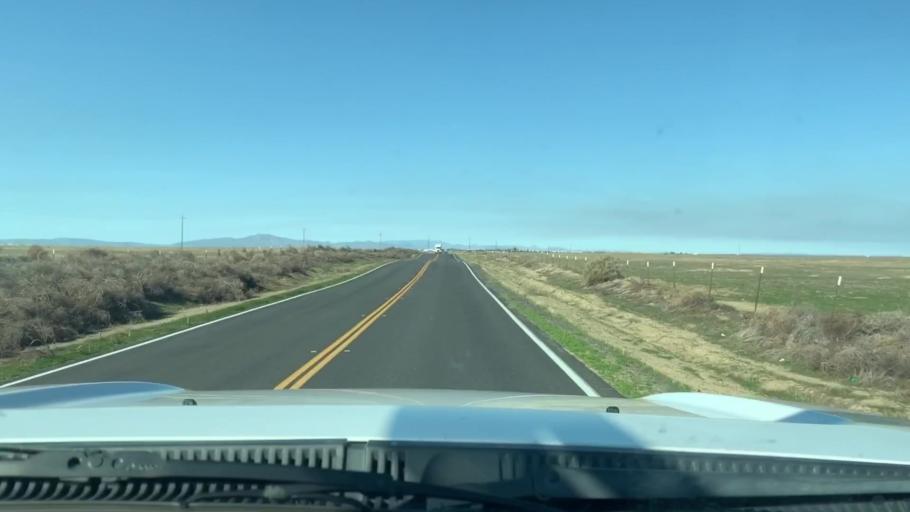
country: US
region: California
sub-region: Kern County
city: Lost Hills
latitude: 35.5860
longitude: -119.8322
